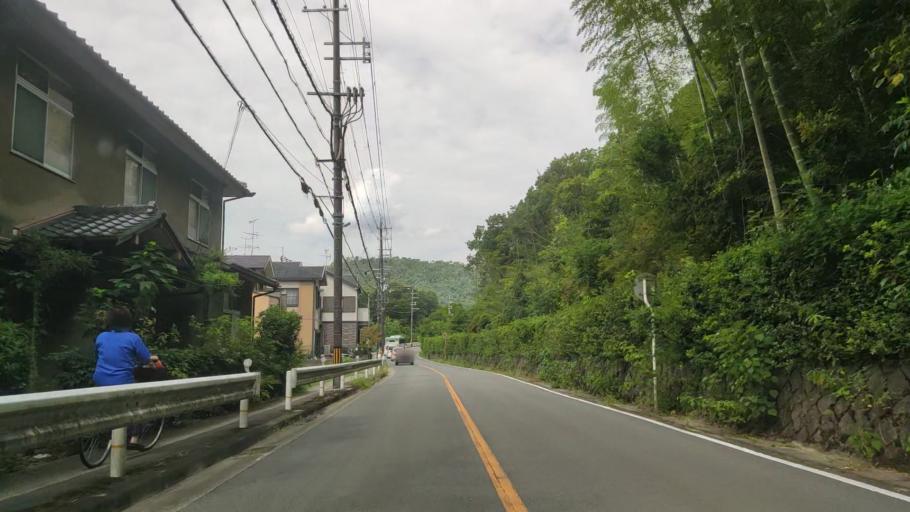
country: JP
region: Kyoto
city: Kyoto
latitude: 35.0250
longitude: 135.6969
